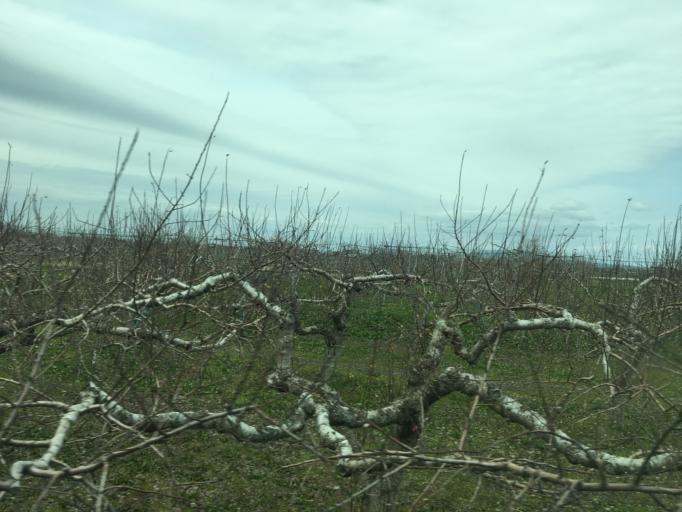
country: JP
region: Aomori
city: Hirosaki
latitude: 40.6438
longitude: 140.5137
